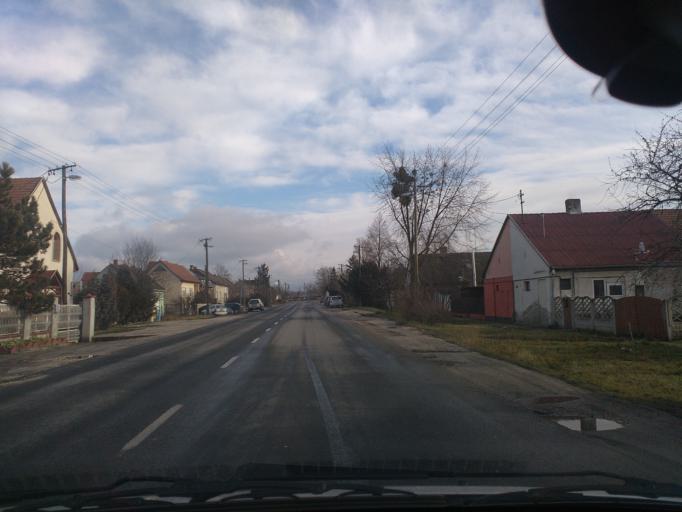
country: HU
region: Komarom-Esztergom
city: Tokod
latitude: 47.7360
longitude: 18.6721
